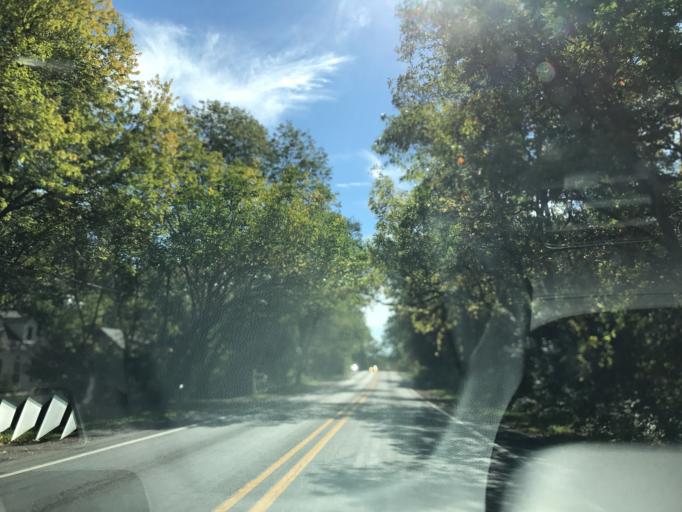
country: US
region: Michigan
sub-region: Washtenaw County
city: Ann Arbor
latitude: 42.3160
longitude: -83.6614
